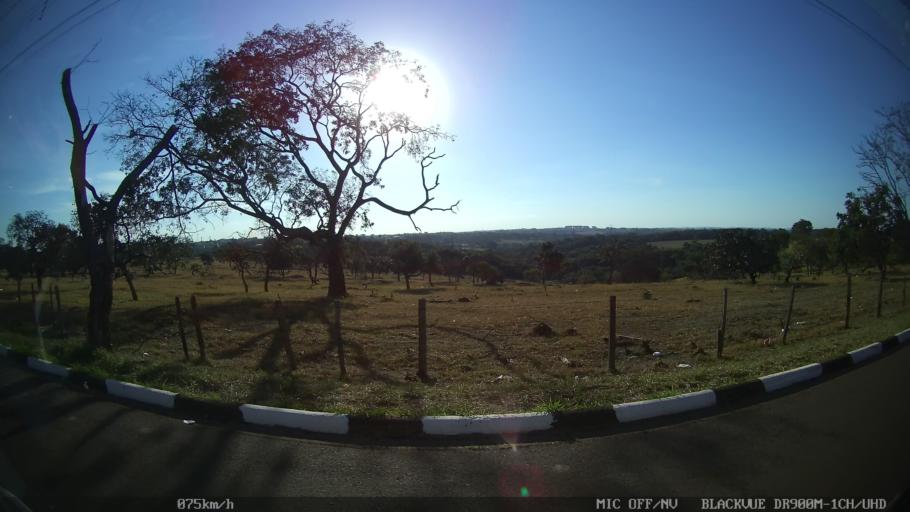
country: BR
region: Sao Paulo
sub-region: Franca
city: Franca
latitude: -20.5115
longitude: -47.3755
